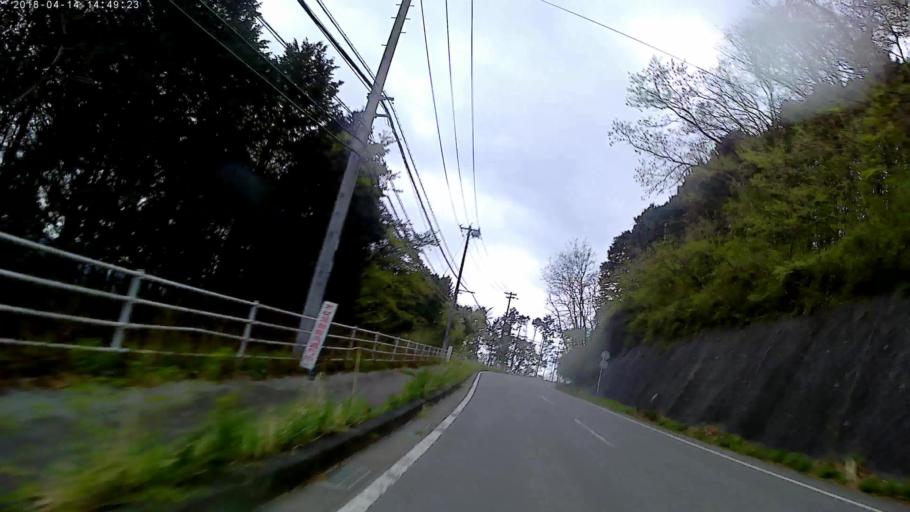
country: JP
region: Shizuoka
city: Gotemba
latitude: 35.3627
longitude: 138.9745
